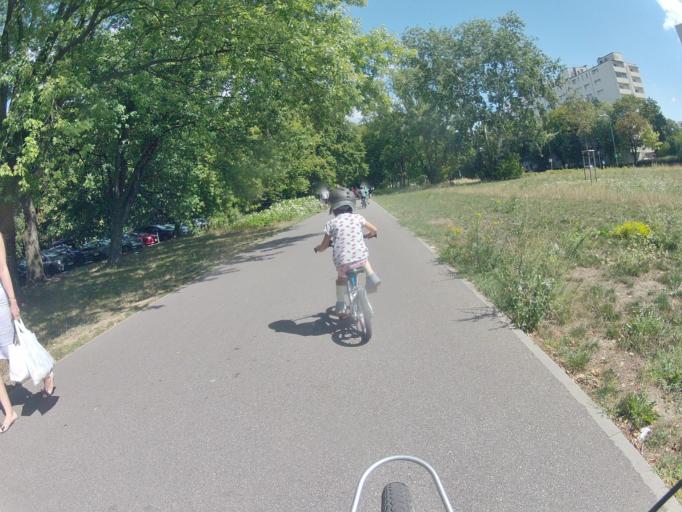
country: PL
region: Masovian Voivodeship
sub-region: Warszawa
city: Ochota
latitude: 52.2095
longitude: 20.9986
